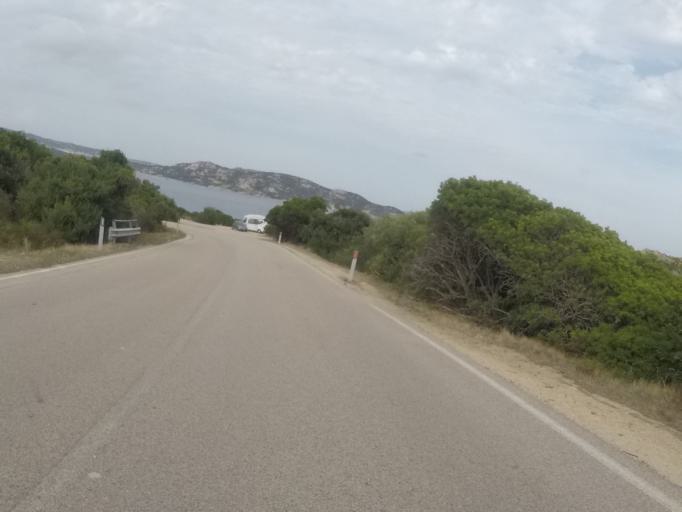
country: IT
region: Sardinia
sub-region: Provincia di Olbia-Tempio
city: Palau
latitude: 41.1732
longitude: 9.4030
